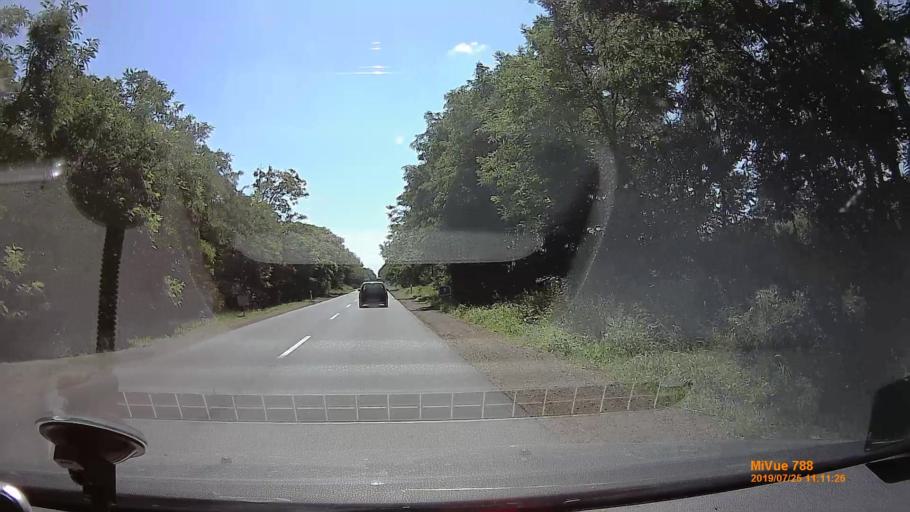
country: HU
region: Szabolcs-Szatmar-Bereg
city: Nagykallo
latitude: 47.9097
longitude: 21.7800
